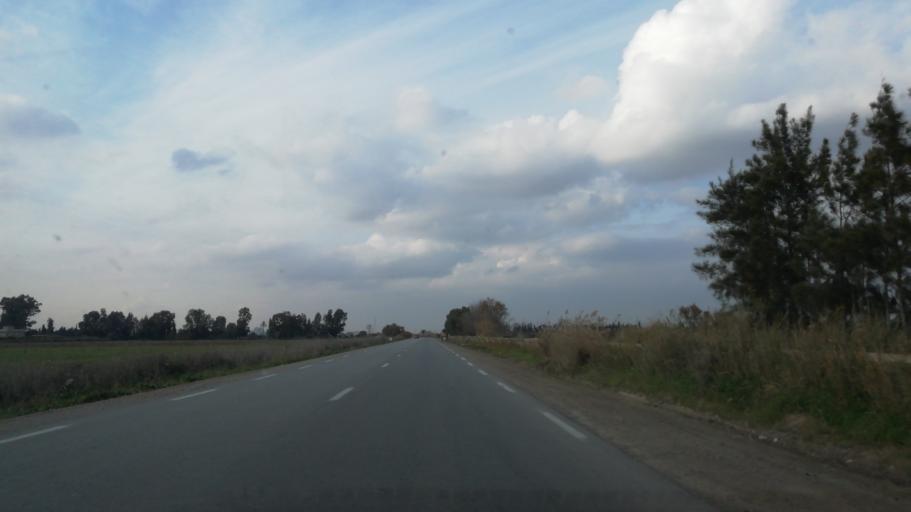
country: DZ
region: Mascara
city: Sig
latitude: 35.6469
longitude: 0.0261
